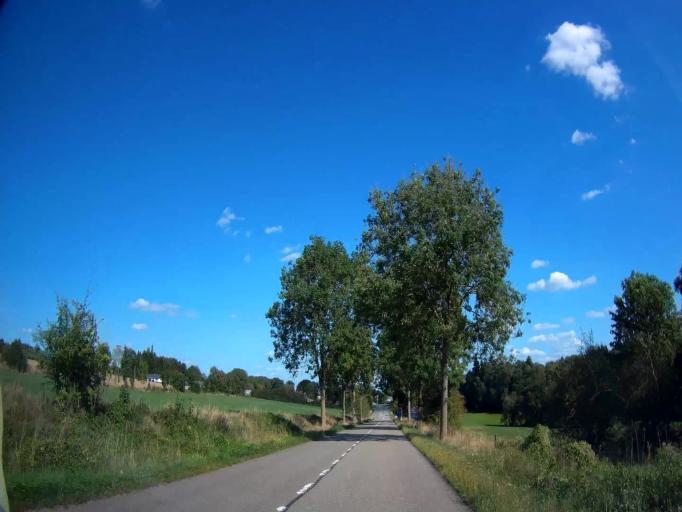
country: BE
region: Wallonia
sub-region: Province de Namur
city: Houyet
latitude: 50.2384
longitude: 4.9841
